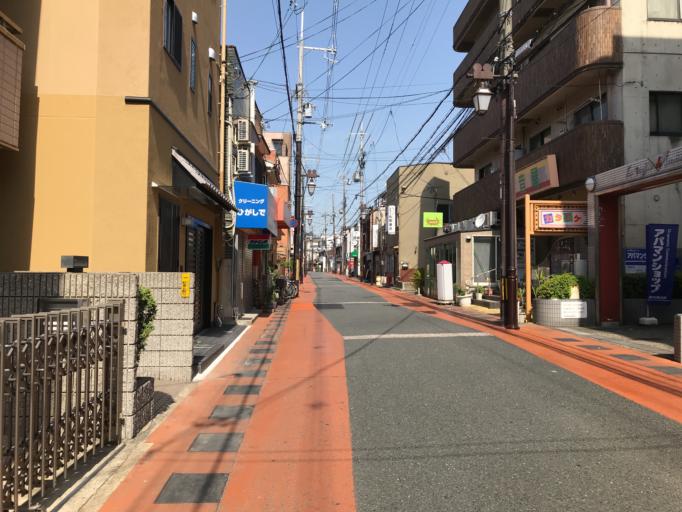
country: JP
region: Kyoto
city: Muko
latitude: 35.0135
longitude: 135.7056
